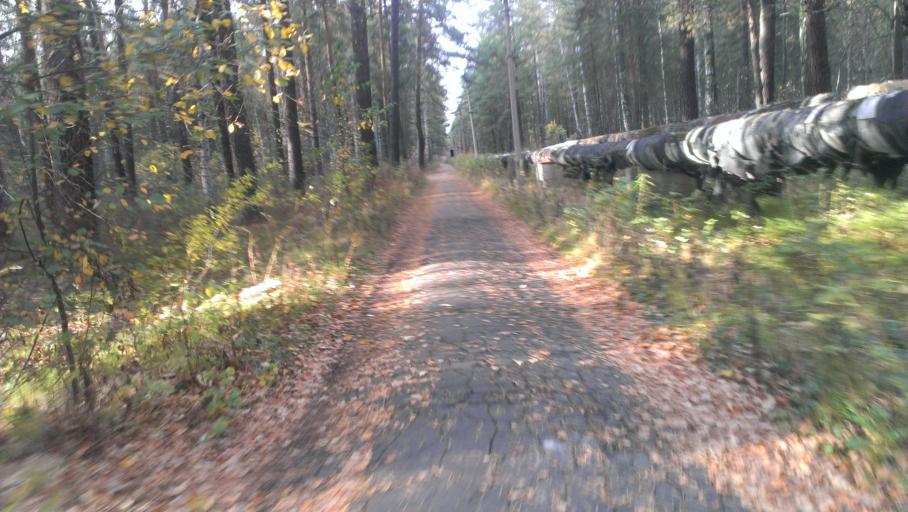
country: RU
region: Altai Krai
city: Yuzhnyy
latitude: 53.2675
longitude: 83.6830
